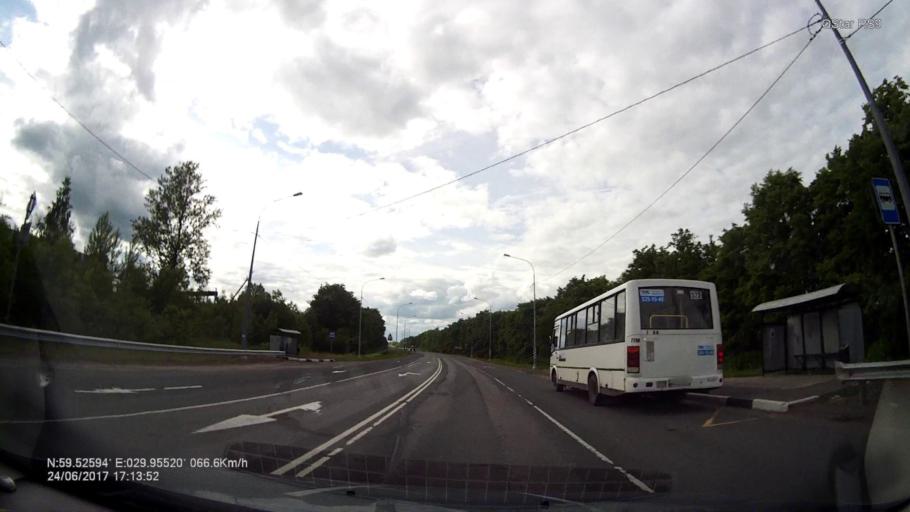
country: RU
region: Leningrad
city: Voyskovitsy
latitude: 59.5262
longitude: 29.9545
